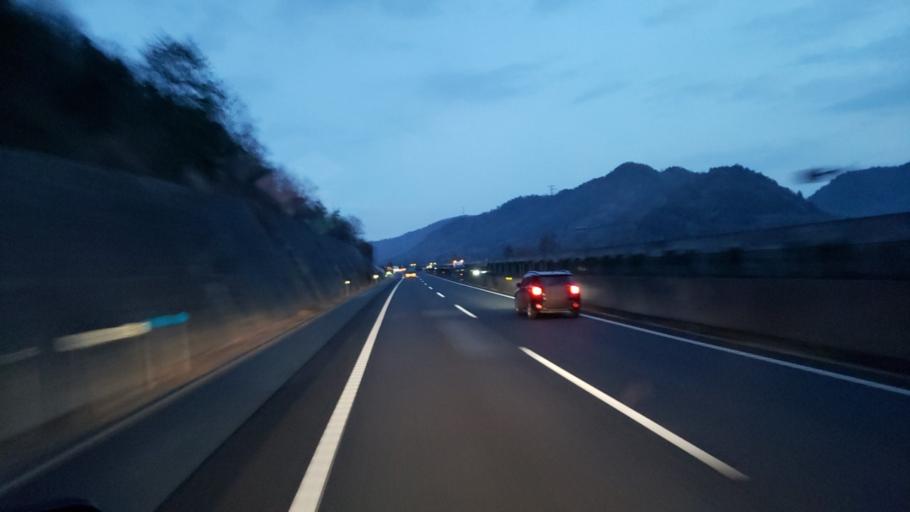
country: JP
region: Hyogo
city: Kakogawacho-honmachi
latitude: 34.8525
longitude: 134.7890
